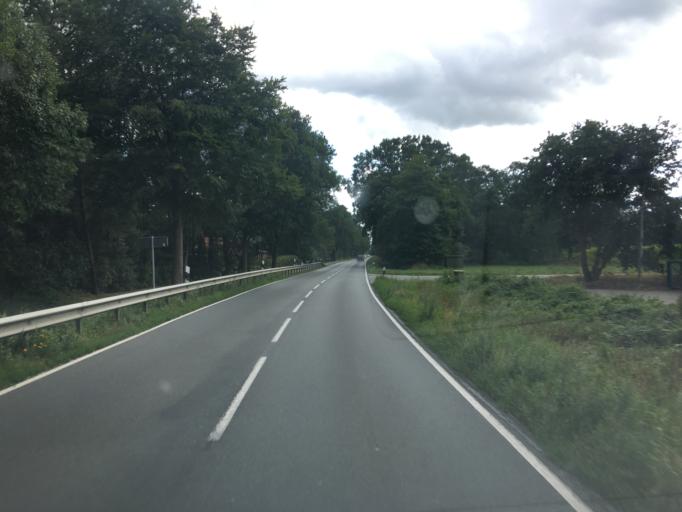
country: DE
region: Lower Saxony
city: Friesoythe
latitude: 53.0682
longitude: 7.8476
